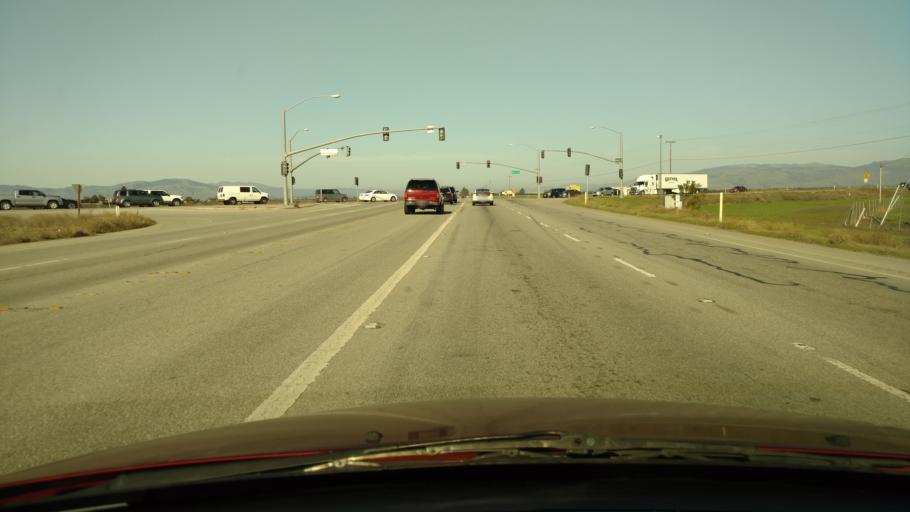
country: US
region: California
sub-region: San Benito County
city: Hollister
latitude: 36.8948
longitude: -121.4265
